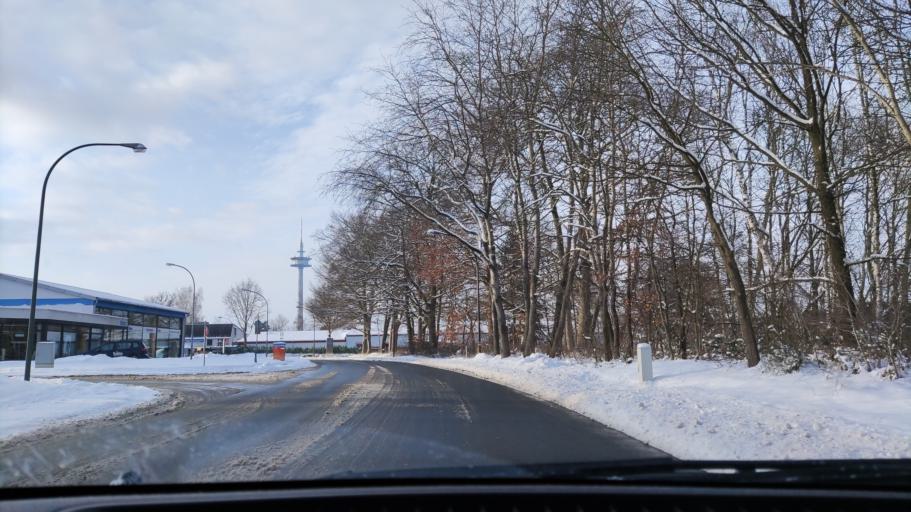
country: DE
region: Lower Saxony
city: Uelzen
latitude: 52.9890
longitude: 10.5420
